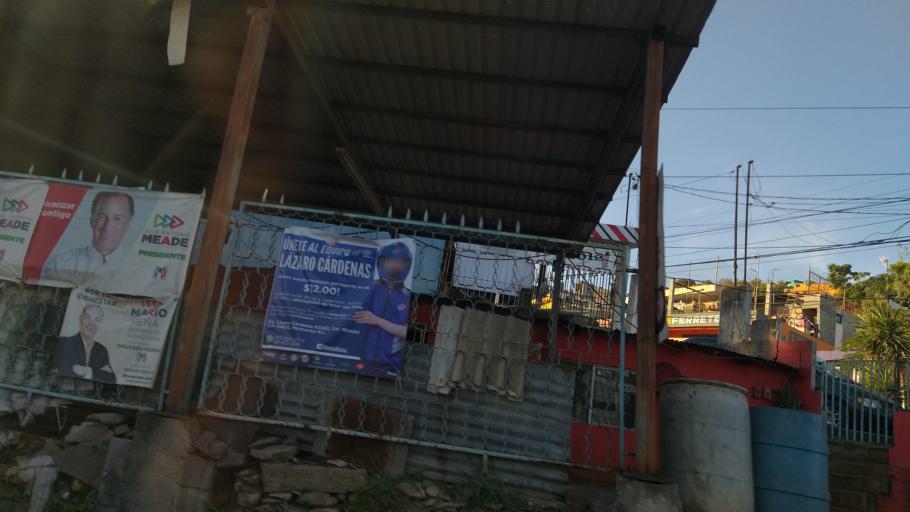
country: MX
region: Nuevo Leon
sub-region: Monterrey
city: Monterrey
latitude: 25.6397
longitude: -100.3066
